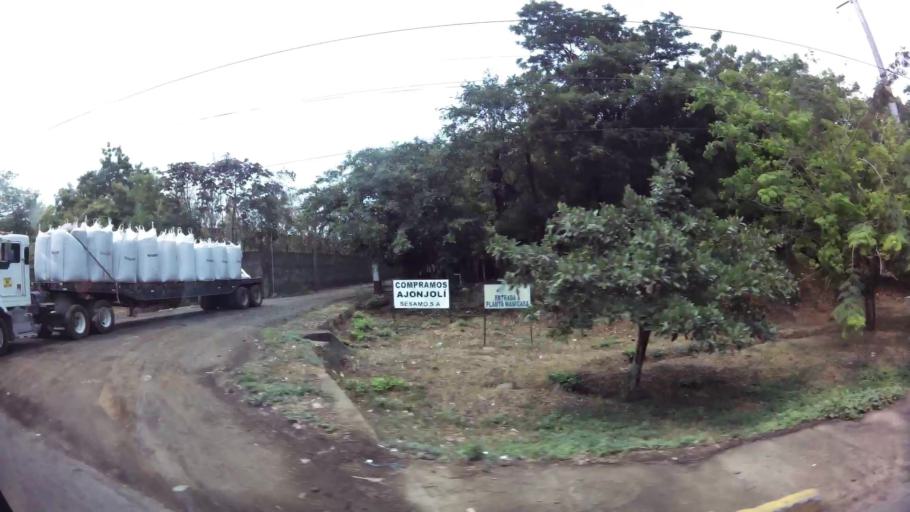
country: NI
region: Chinandega
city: Chinandega
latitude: 12.6392
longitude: -87.1272
